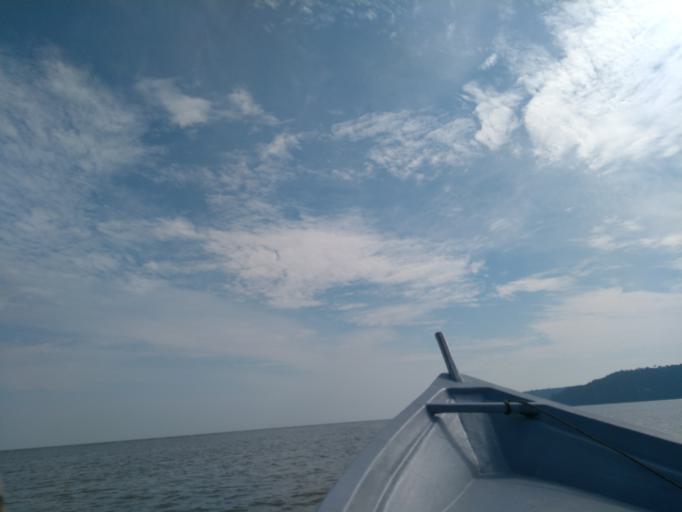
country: MY
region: Sarawak
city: Kuching
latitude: 1.7010
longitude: 110.4293
